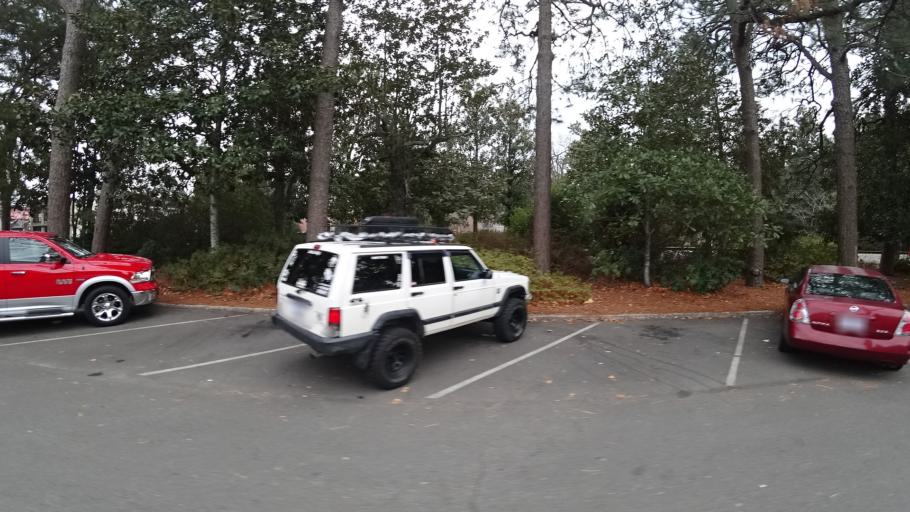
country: US
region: North Carolina
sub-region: Moore County
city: Southern Pines
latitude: 35.1738
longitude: -79.3924
